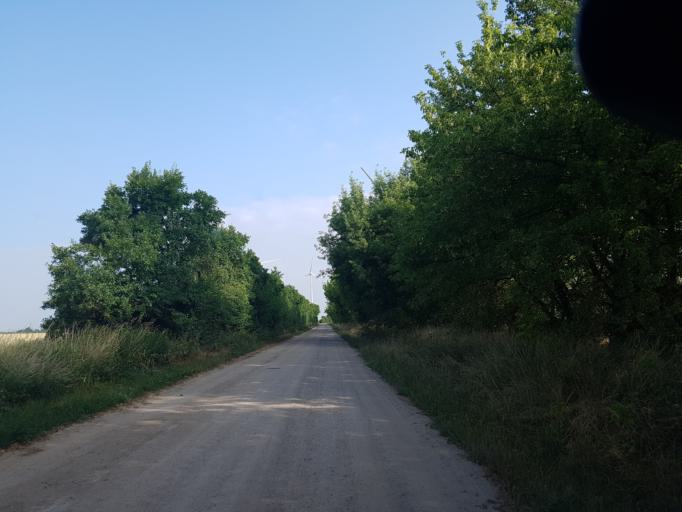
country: DE
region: Saxony-Anhalt
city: Kropstadt
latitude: 51.9908
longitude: 12.8188
